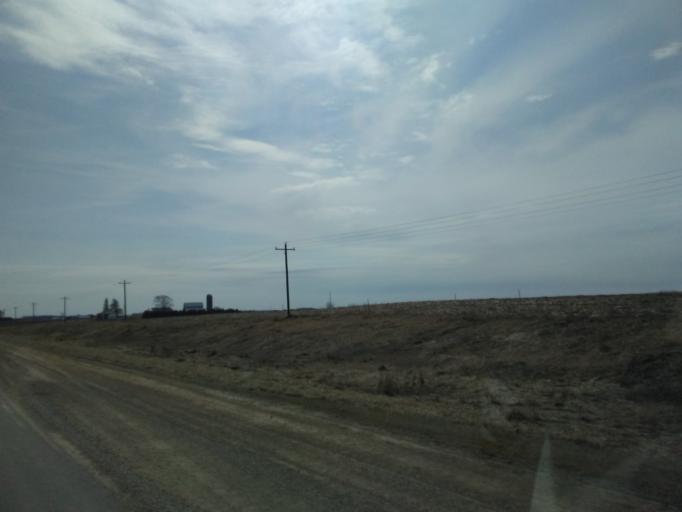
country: US
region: Iowa
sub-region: Winneshiek County
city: Decorah
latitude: 43.4423
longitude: -91.8619
